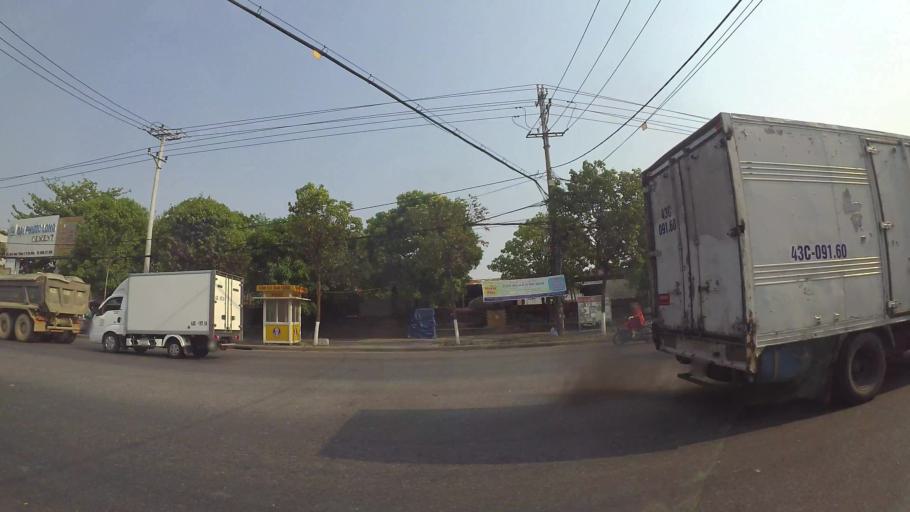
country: VN
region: Da Nang
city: Cam Le
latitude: 16.0148
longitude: 108.2001
